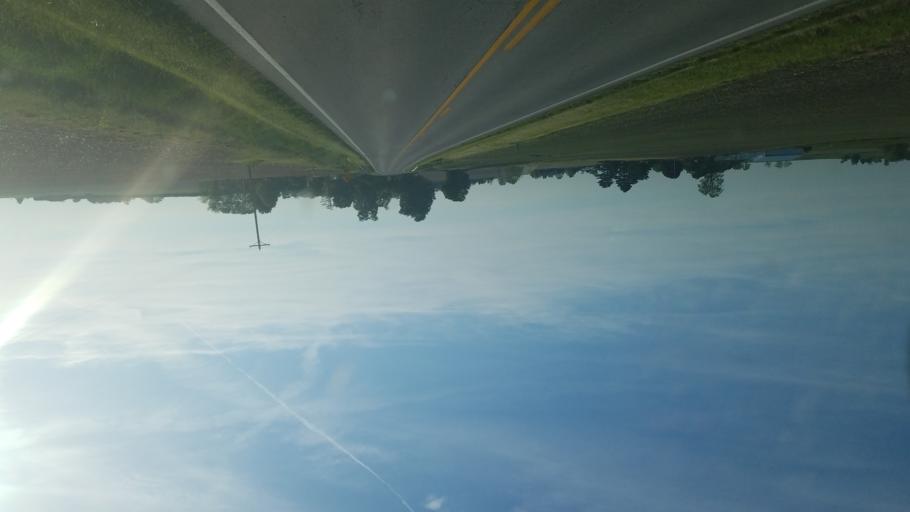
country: US
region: Ohio
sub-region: Highland County
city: Greenfield
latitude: 39.4023
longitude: -83.3095
